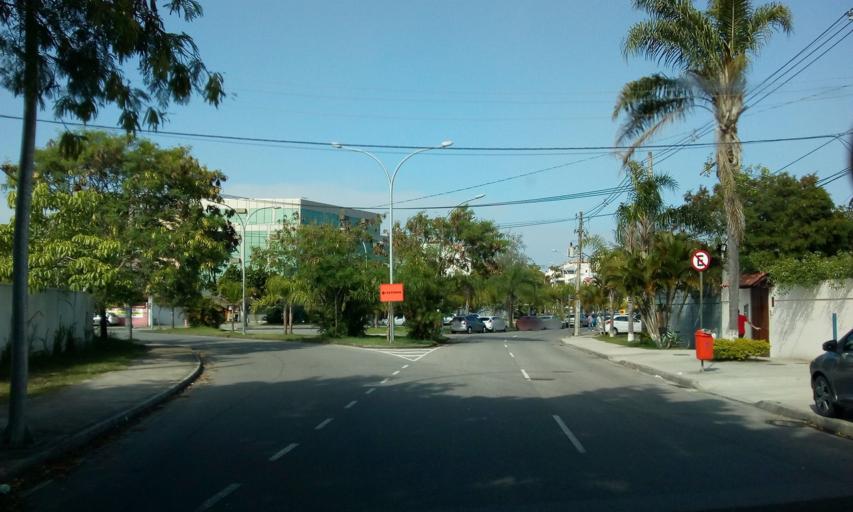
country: BR
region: Rio de Janeiro
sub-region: Nilopolis
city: Nilopolis
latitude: -23.0125
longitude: -43.4458
